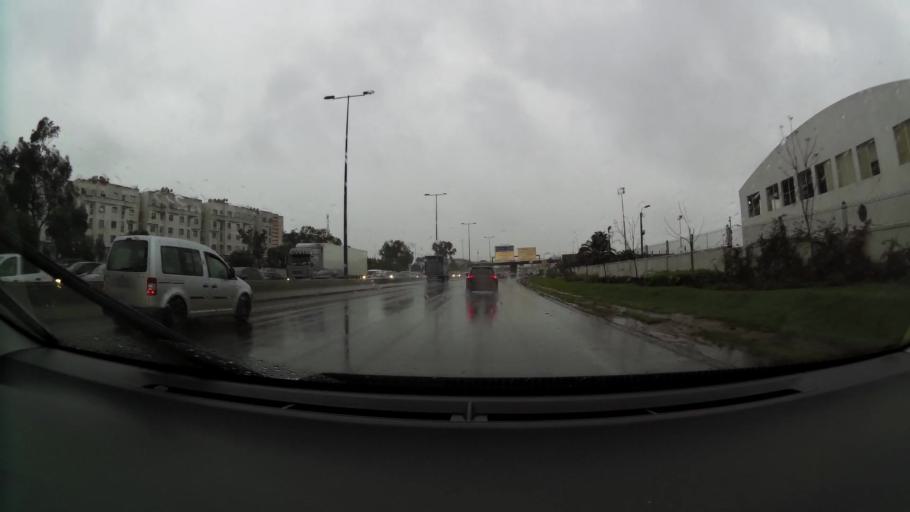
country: MA
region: Grand Casablanca
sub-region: Casablanca
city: Casablanca
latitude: 33.5618
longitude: -7.5857
